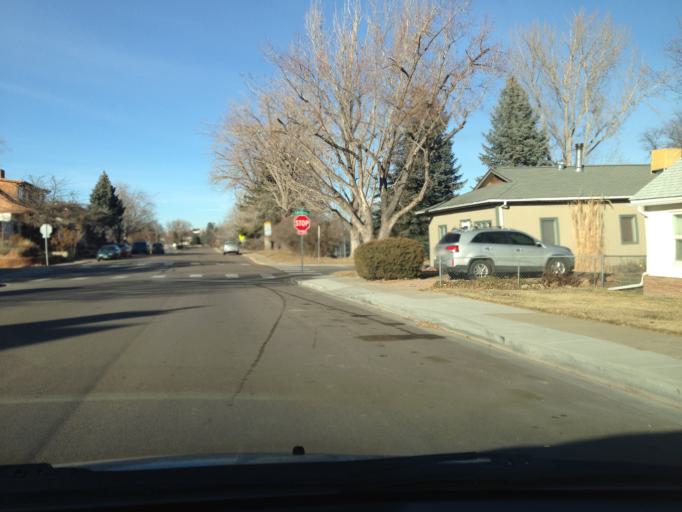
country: US
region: Colorado
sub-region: Boulder County
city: Louisville
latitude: 39.9822
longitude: -105.1346
